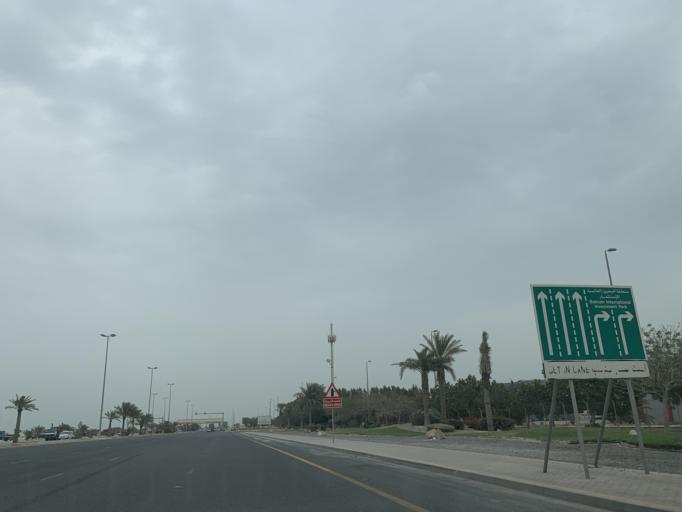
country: BH
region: Muharraq
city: Al Hadd
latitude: 26.2251
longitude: 50.6713
